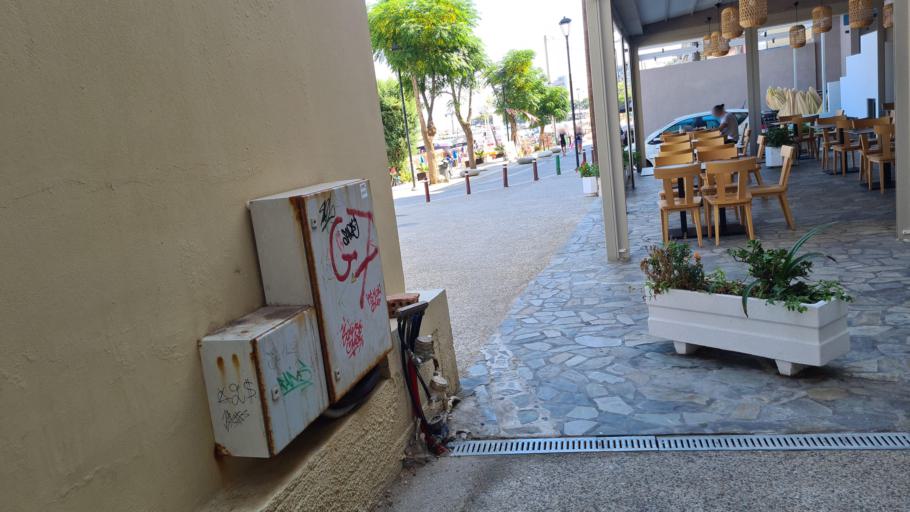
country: GR
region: Crete
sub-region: Nomos Chanias
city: Chania
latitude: 35.5131
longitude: 24.0060
